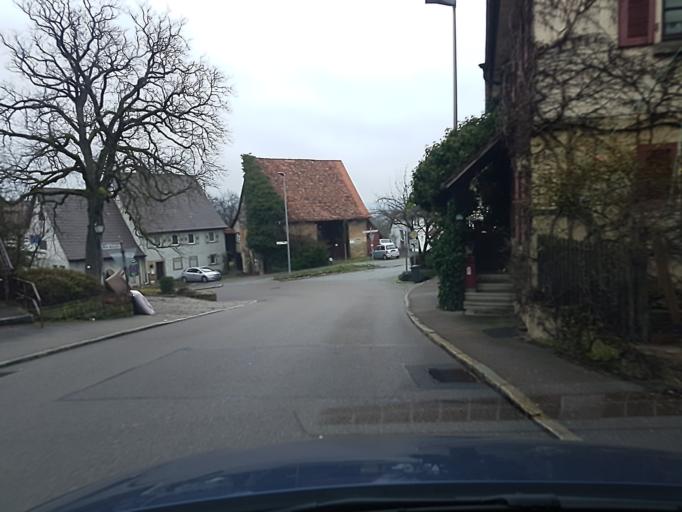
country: DE
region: Baden-Wuerttemberg
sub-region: Regierungsbezirk Stuttgart
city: Freiberg am Neckar
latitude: 48.9392
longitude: 9.1863
